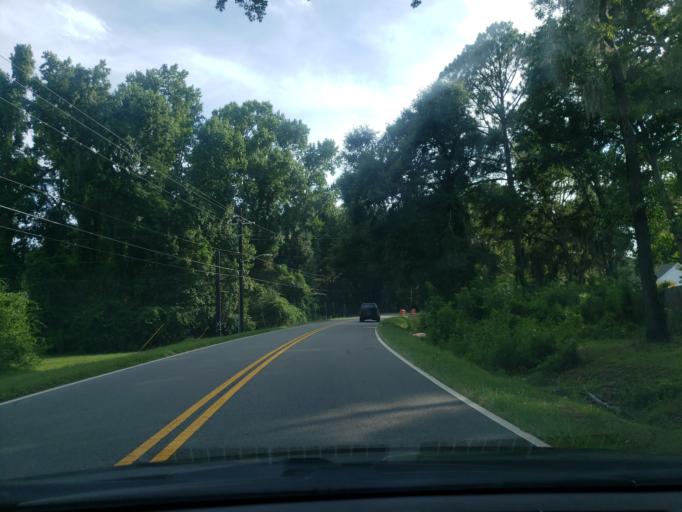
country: US
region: Georgia
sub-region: Chatham County
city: Montgomery
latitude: 31.9601
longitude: -81.1371
